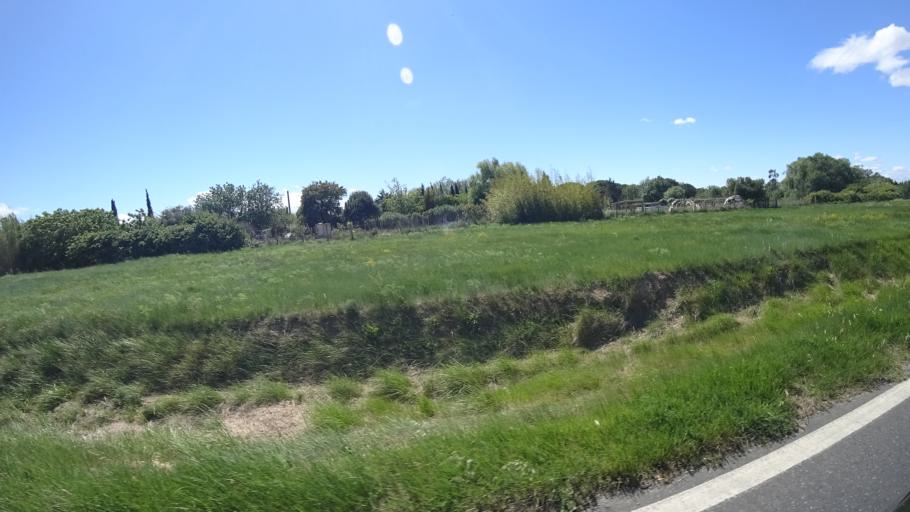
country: FR
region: Languedoc-Roussillon
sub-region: Departement des Pyrenees-Orientales
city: Saint-Nazaire
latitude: 42.6661
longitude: 2.9803
